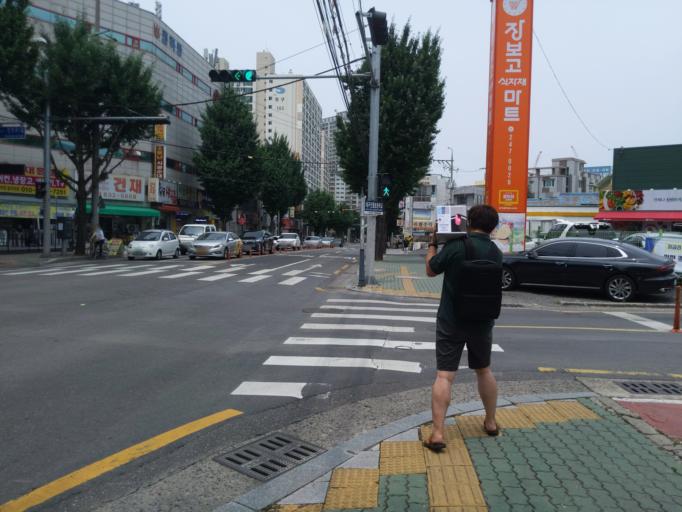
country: KR
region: Daegu
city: Hwawon
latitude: 35.8106
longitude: 128.5261
